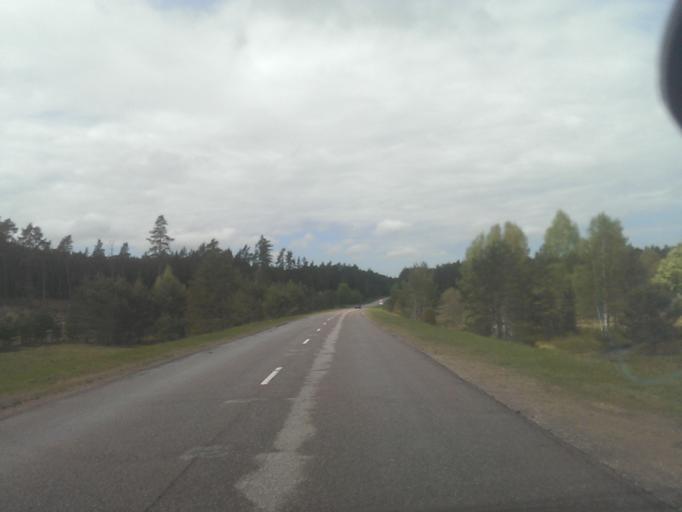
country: LV
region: Ventspils Rajons
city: Piltene
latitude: 57.0745
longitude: 21.7931
